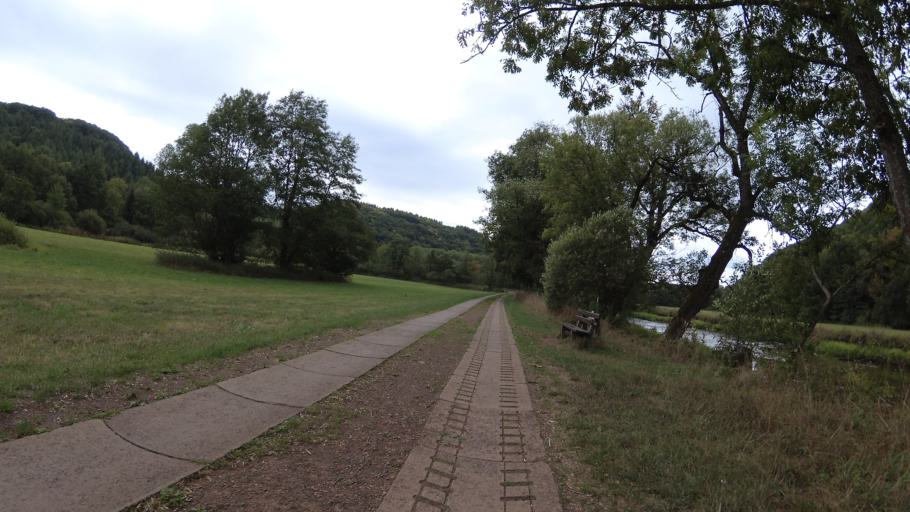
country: DE
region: Saarland
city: Wadern
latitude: 49.5154
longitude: 6.8834
